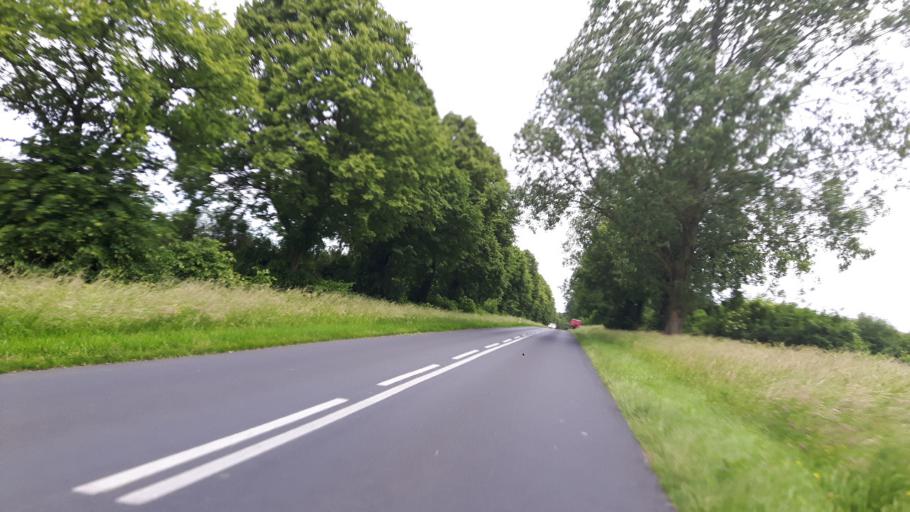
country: PL
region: West Pomeranian Voivodeship
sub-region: Powiat gryficki
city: Trzebiatow
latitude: 54.0016
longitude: 15.2401
